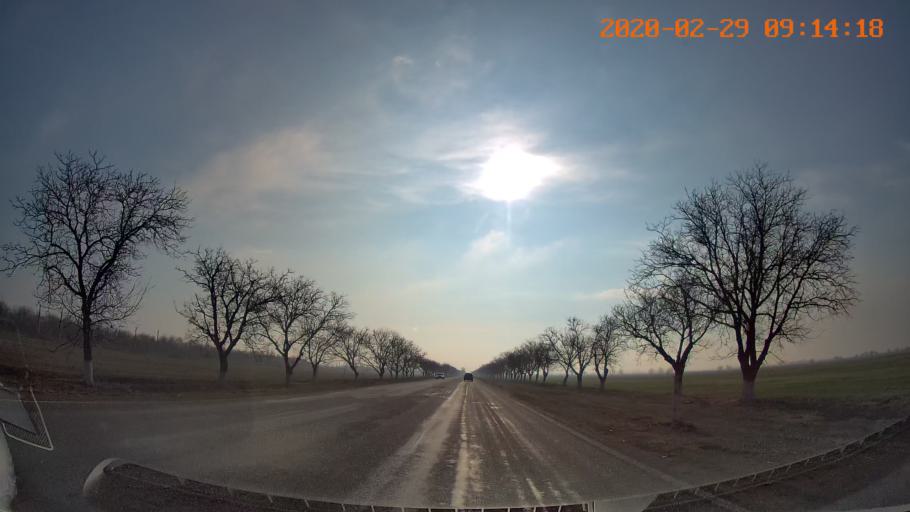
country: MD
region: Telenesti
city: Pervomaisc
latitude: 46.8098
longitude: 29.8506
